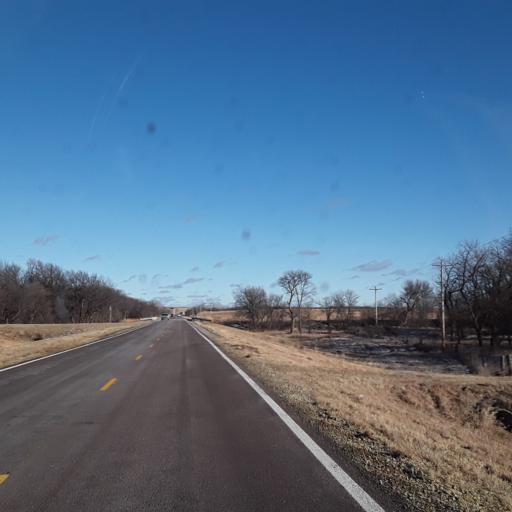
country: US
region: Kansas
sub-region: Cloud County
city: Concordia
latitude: 39.4962
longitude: -97.7434
